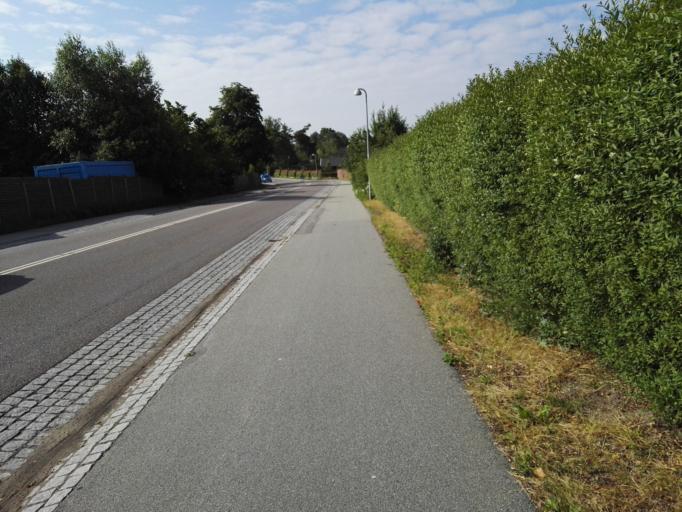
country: DK
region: Zealand
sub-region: Roskilde Kommune
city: Jyllinge
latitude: 55.7685
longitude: 12.1096
